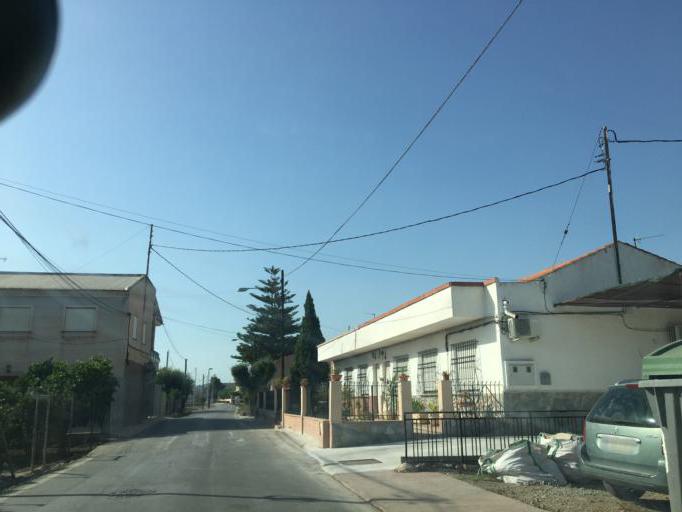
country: ES
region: Murcia
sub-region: Murcia
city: Santomera
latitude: 38.0291
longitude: -1.0663
